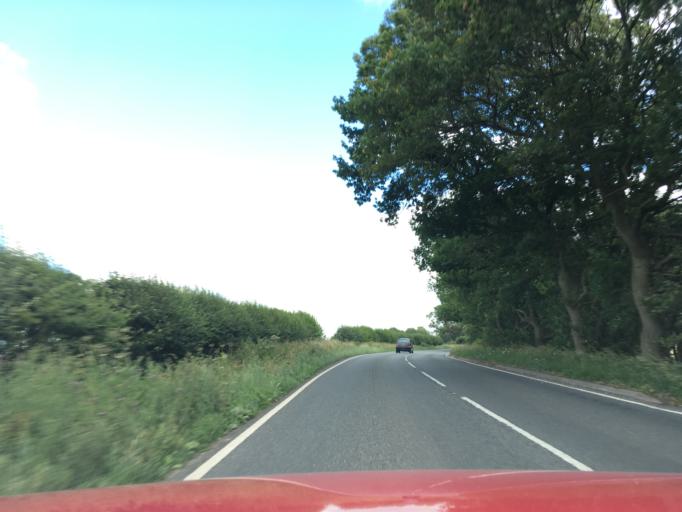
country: GB
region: England
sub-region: Leicestershire
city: Measham
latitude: 52.6510
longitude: -1.5141
